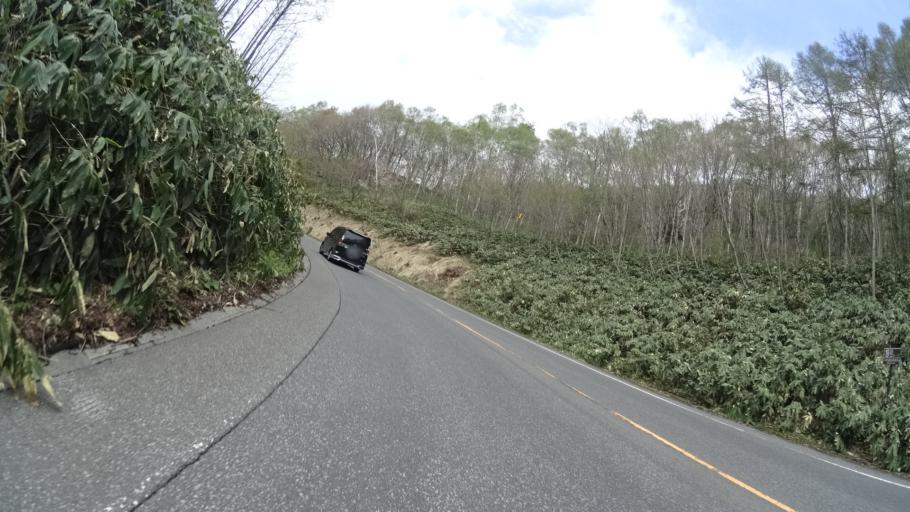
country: JP
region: Nagano
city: Nakano
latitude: 36.7228
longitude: 138.4742
